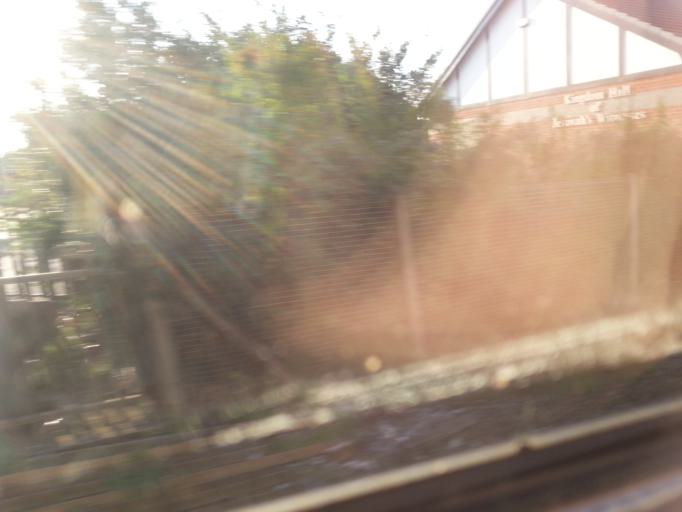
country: GB
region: England
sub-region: Sefton
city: Formby
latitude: 53.5513
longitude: -3.0706
